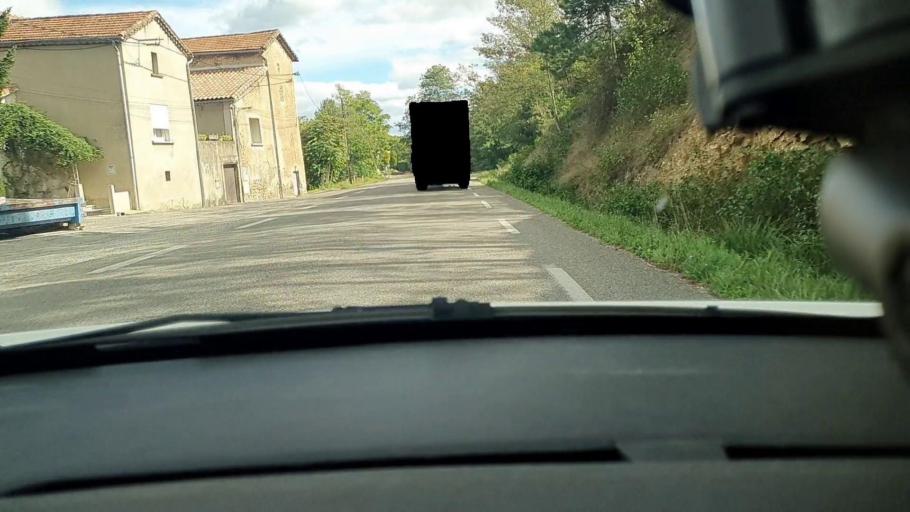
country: FR
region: Languedoc-Roussillon
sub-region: Departement du Gard
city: Saint-Florent-sur-Auzonnet
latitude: 44.2460
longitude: 4.0962
